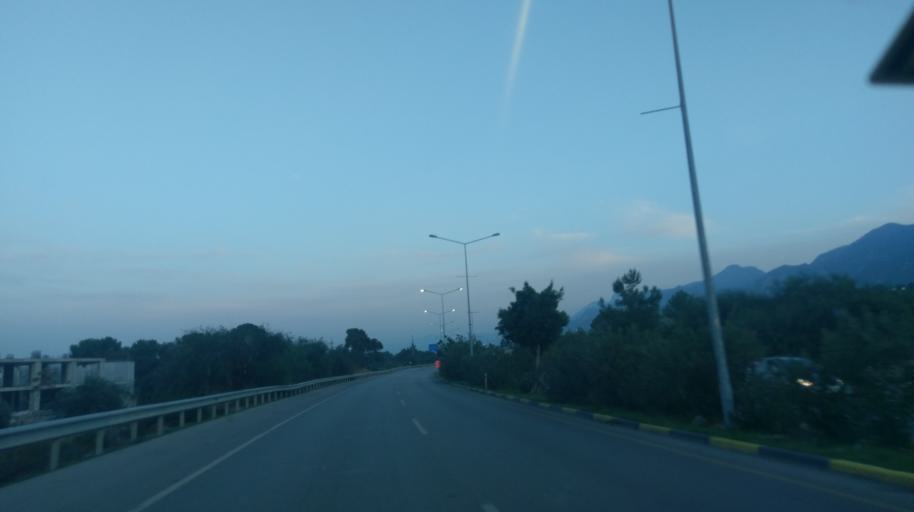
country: CY
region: Keryneia
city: Kyrenia
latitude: 35.3276
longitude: 33.3119
